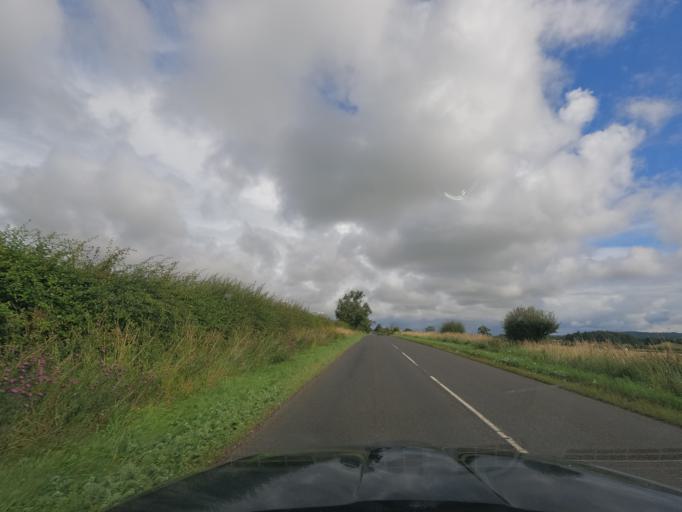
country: GB
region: England
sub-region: Northumberland
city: Lowick
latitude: 55.6208
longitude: -1.9905
